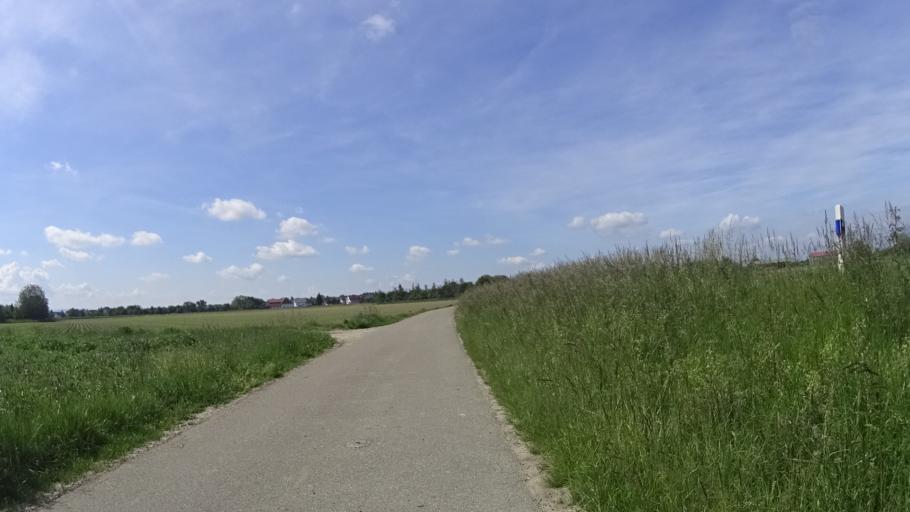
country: DE
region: Baden-Wuerttemberg
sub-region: Freiburg Region
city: Schutterwald
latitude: 48.4751
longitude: 7.8137
